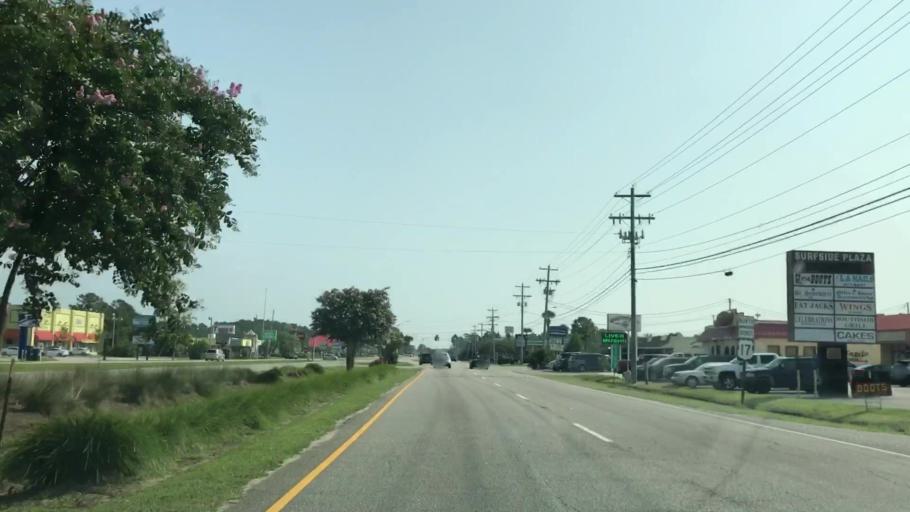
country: US
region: South Carolina
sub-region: Horry County
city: Surfside Beach
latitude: 33.6145
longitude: -78.9790
